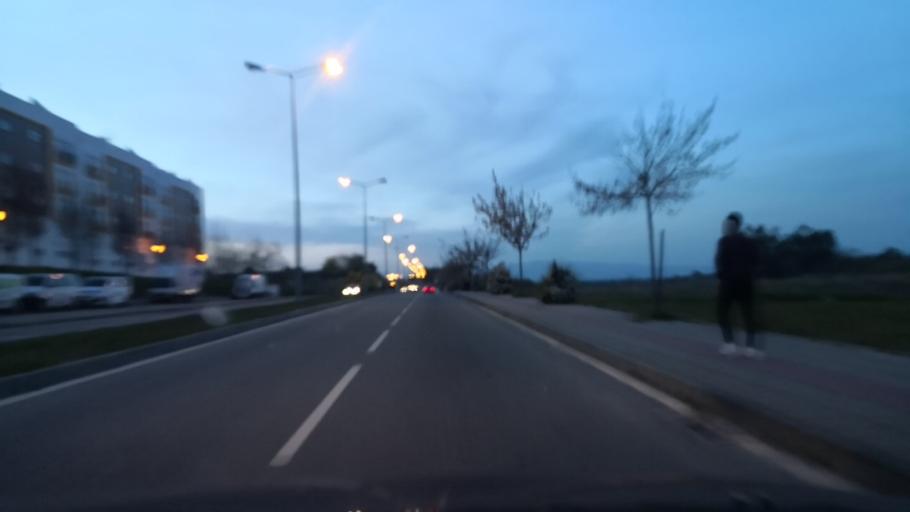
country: PT
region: Castelo Branco
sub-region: Castelo Branco
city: Castelo Branco
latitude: 39.8265
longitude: -7.4849
